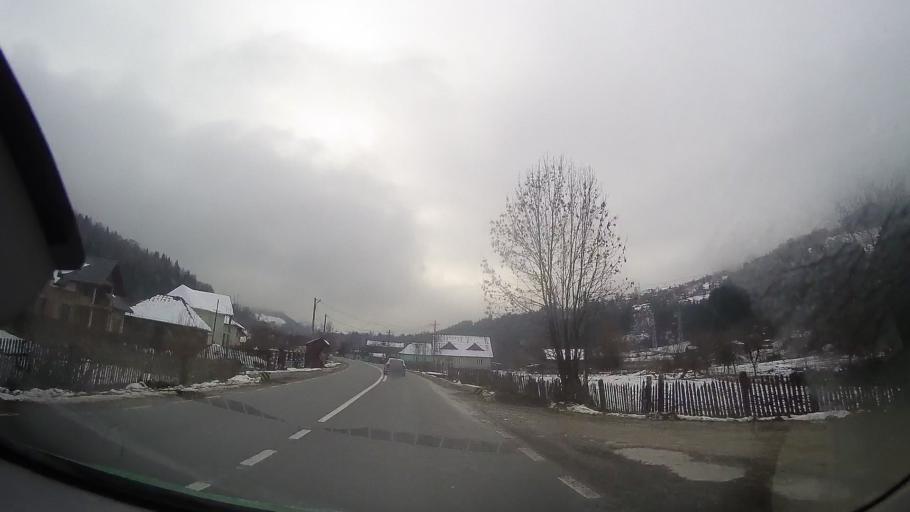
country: RO
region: Neamt
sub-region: Comuna Bicazu Ardelean
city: Bicazu Ardelean
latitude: 46.8666
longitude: 25.9419
